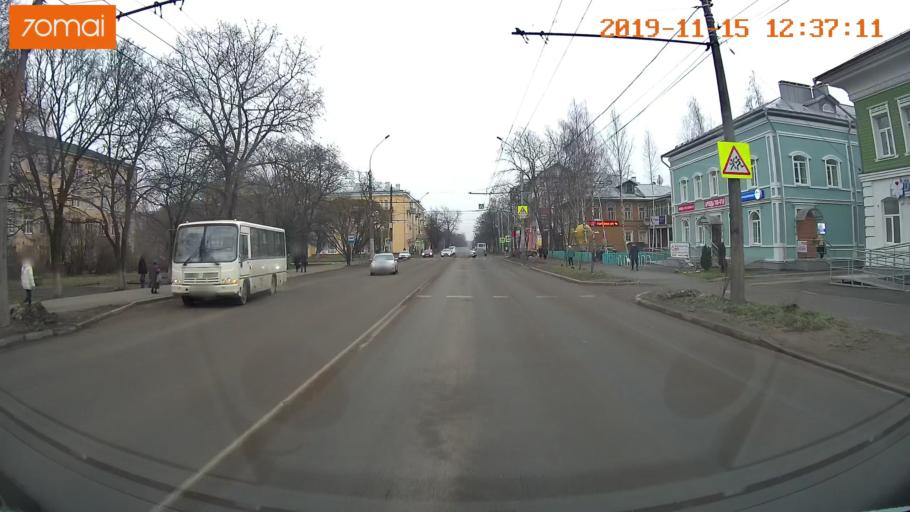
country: RU
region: Vologda
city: Vologda
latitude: 59.2107
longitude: 39.8961
